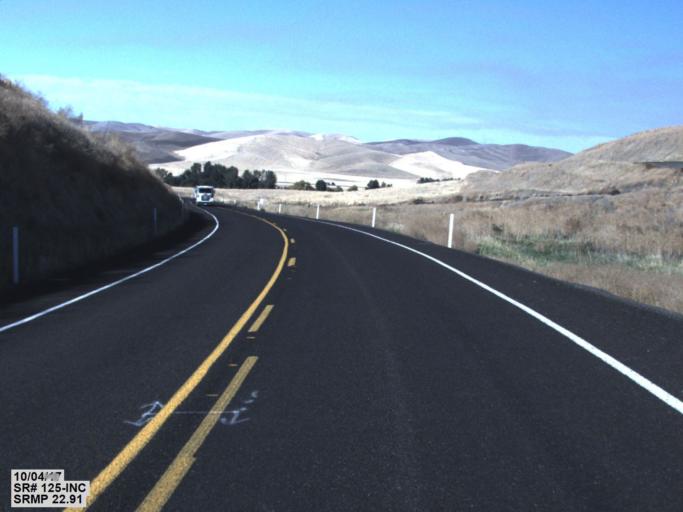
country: US
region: Washington
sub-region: Walla Walla County
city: Waitsburg
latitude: 46.2878
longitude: -118.3397
